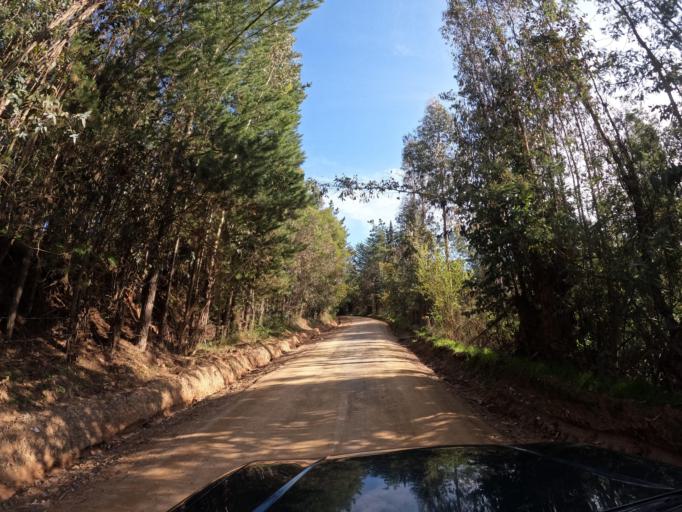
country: CL
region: Biobio
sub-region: Provincia de Biobio
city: La Laja
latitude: -37.1381
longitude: -72.7270
